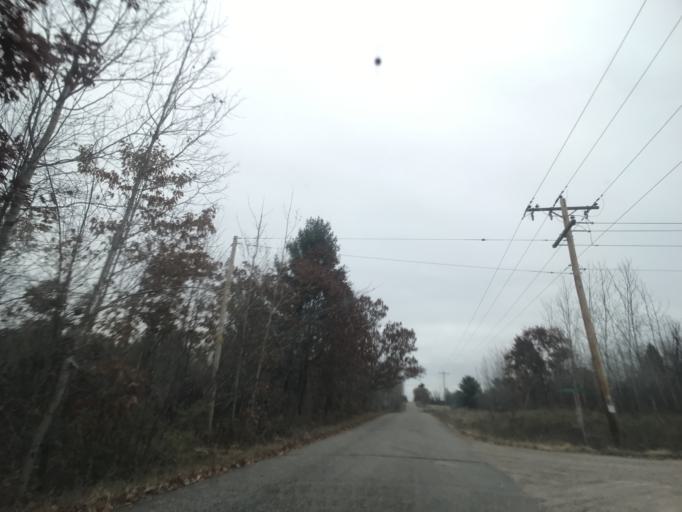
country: US
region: Wisconsin
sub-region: Menominee County
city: Legend Lake
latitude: 45.1687
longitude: -88.4559
